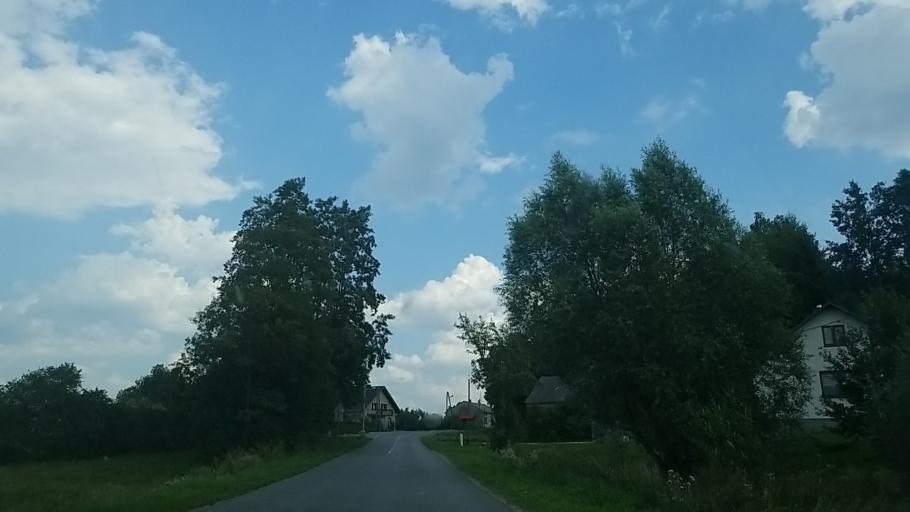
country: PL
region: Lublin Voivodeship
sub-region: Powiat bilgorajski
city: Goraj
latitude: 50.7239
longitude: 22.6576
